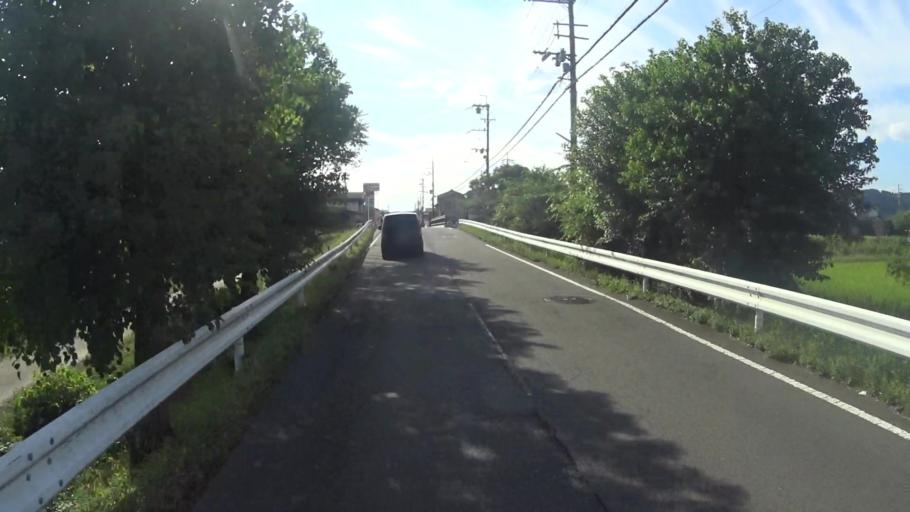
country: JP
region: Kyoto
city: Yawata
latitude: 34.8661
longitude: 135.7139
